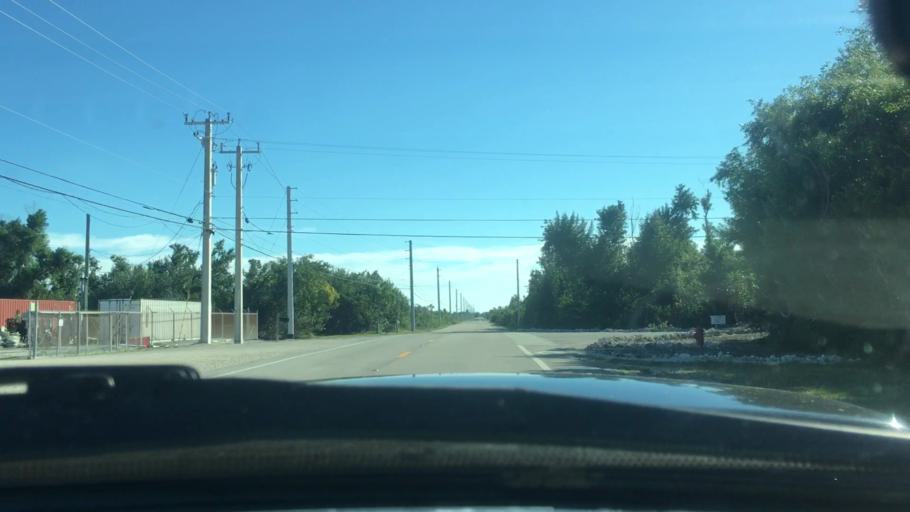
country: US
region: Florida
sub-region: Monroe County
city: Cudjoe Key
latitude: 24.6780
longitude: -81.4996
